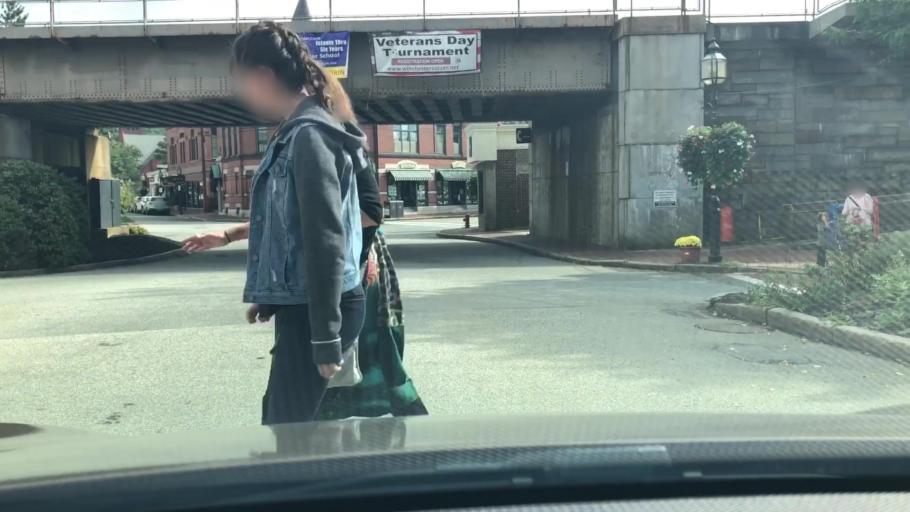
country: US
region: Massachusetts
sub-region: Middlesex County
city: Winchester
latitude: 42.4526
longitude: -71.1376
